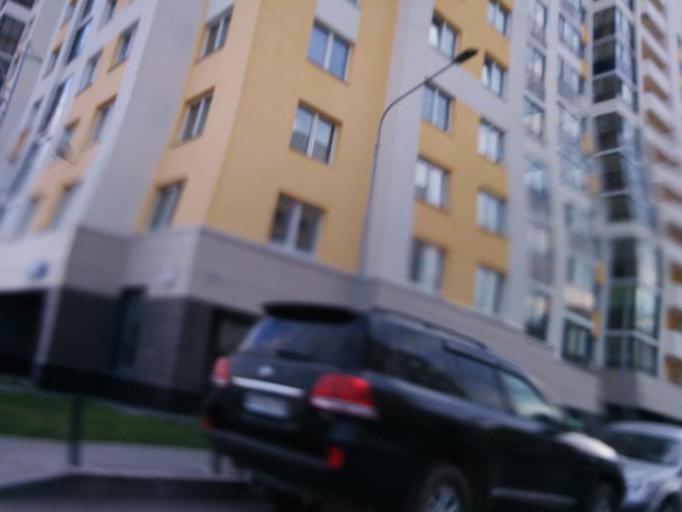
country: RU
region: Sverdlovsk
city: Sovkhoznyy
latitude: 56.7859
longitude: 60.5249
